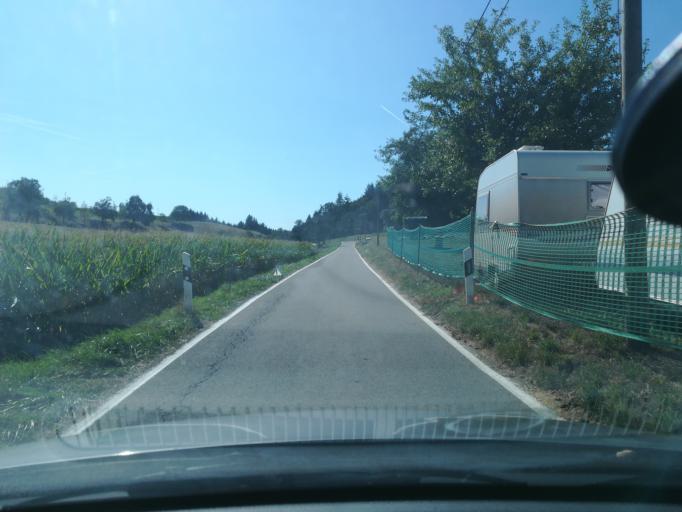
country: DE
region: Baden-Wuerttemberg
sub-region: Freiburg Region
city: Ohningen
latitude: 47.6900
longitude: 8.8934
